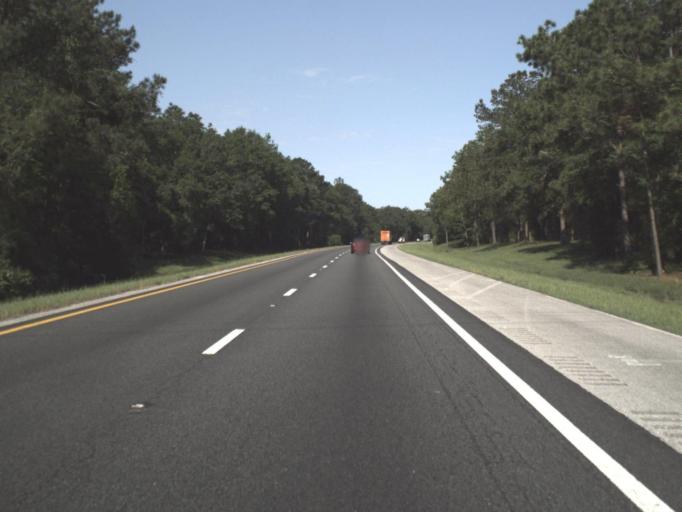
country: US
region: Florida
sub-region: Holmes County
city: Bonifay
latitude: 30.7612
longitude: -85.7276
